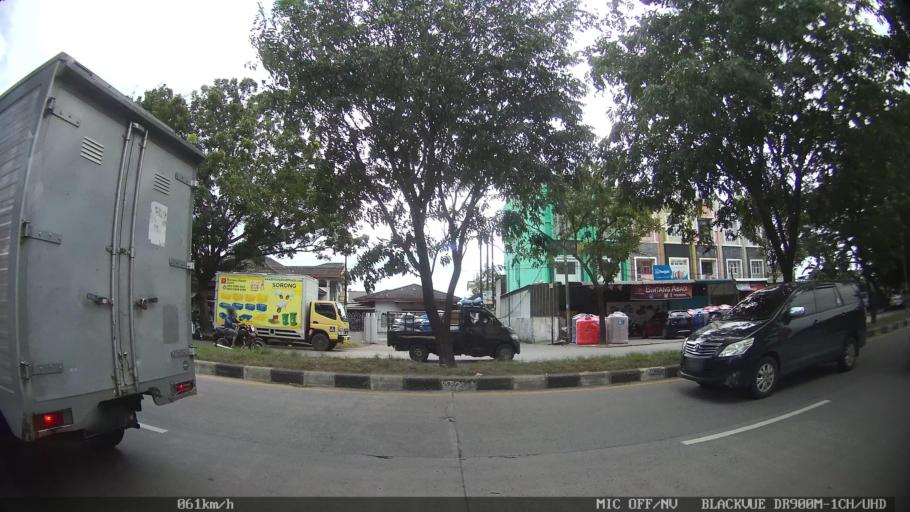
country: ID
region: North Sumatra
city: Medan
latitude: 3.6300
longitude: 98.6773
